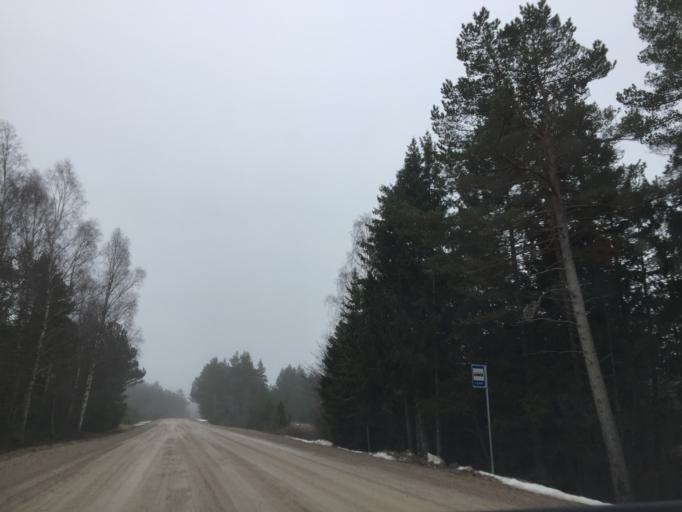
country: EE
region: Saare
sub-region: Kuressaare linn
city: Kuressaare
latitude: 58.4789
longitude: 22.0007
